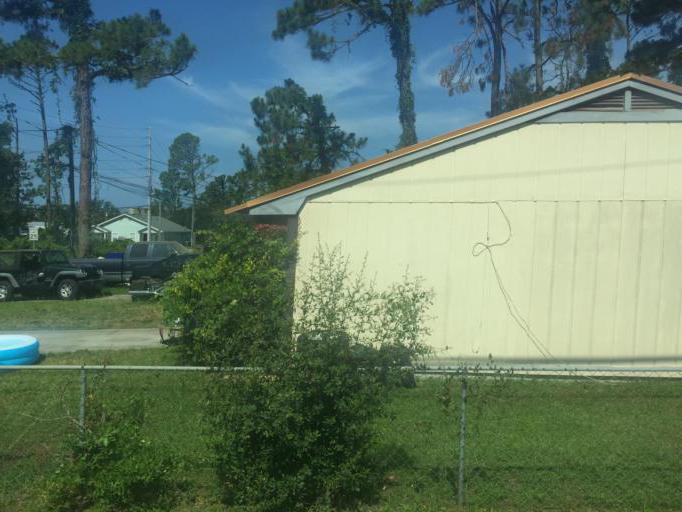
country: US
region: Florida
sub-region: Bay County
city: Lower Grand Lagoon
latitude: 30.1584
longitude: -85.7551
